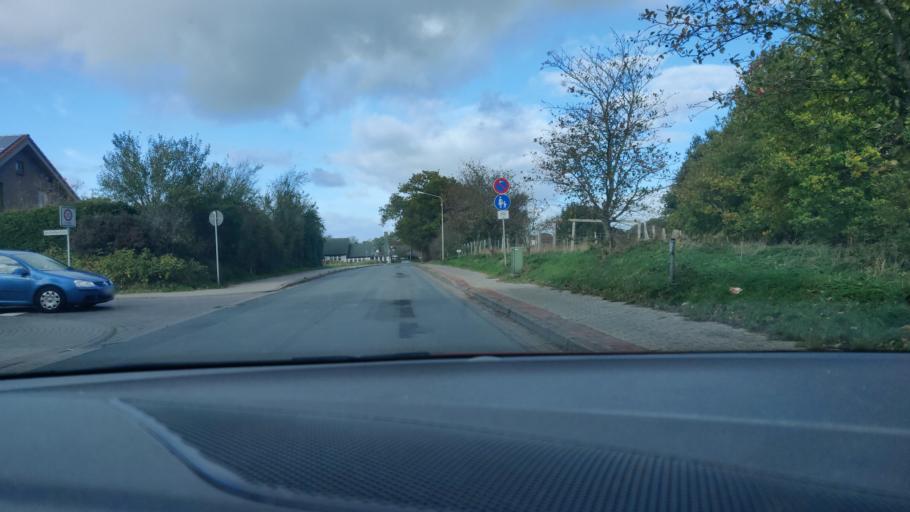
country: DE
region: Lower Saxony
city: Cuxhaven
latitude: 53.8597
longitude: 8.6370
